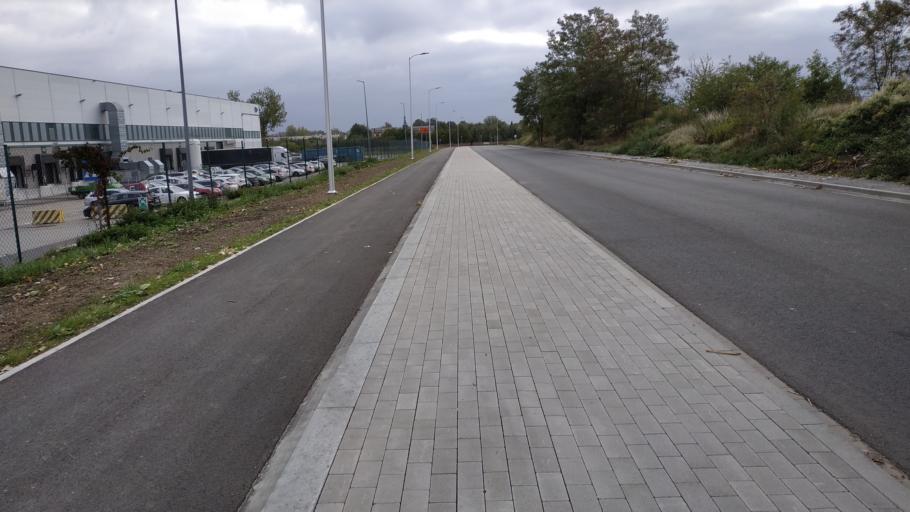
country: PL
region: Lower Silesian Voivodeship
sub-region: Powiat wroclawski
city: Bielany Wroclawskie
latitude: 51.0406
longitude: 16.9586
